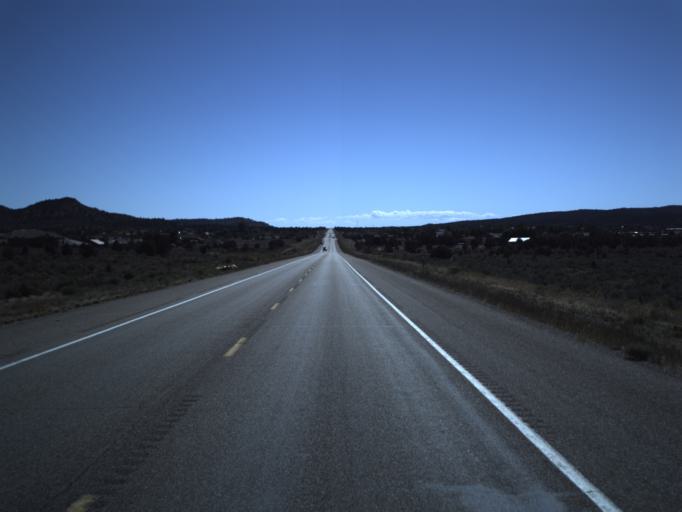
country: US
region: Utah
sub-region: Washington County
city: Ivins
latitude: 37.3146
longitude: -113.6772
